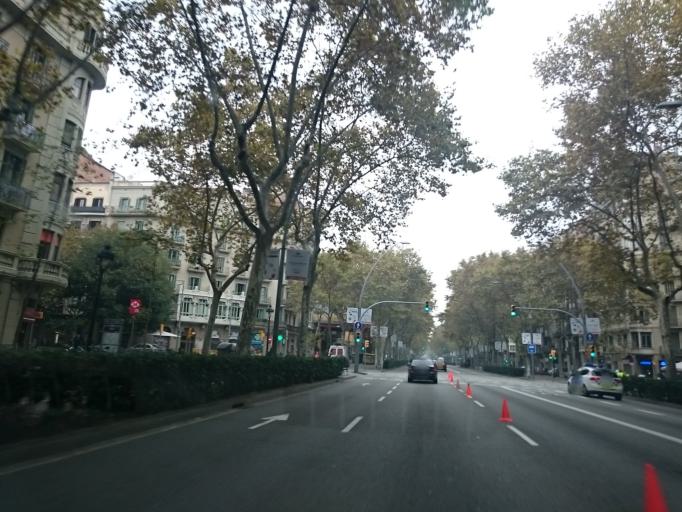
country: ES
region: Catalonia
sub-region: Provincia de Barcelona
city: Sants-Montjuic
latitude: 41.3793
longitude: 2.1547
